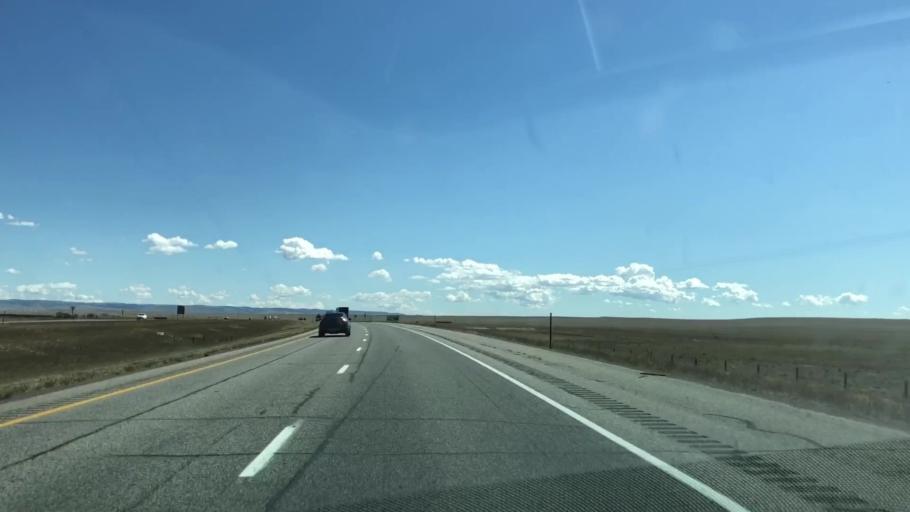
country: US
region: Wyoming
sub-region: Albany County
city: Laramie
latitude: 41.3810
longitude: -105.8115
